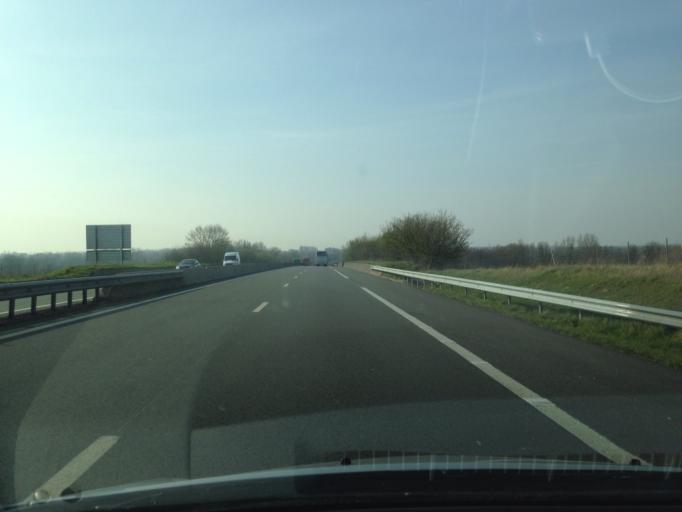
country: FR
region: Picardie
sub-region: Departement de la Somme
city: Rue
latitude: 50.3303
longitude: 1.7078
